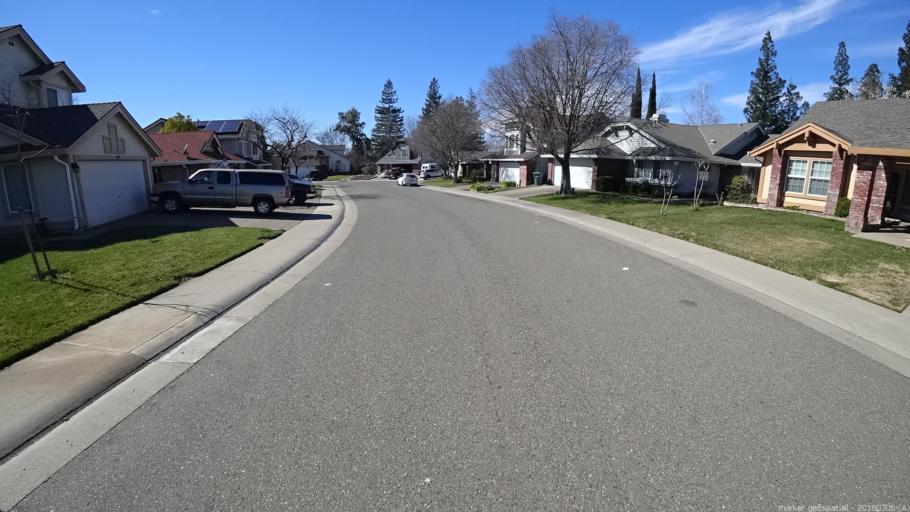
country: US
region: California
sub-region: Sacramento County
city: Vineyard
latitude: 38.4641
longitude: -121.3612
